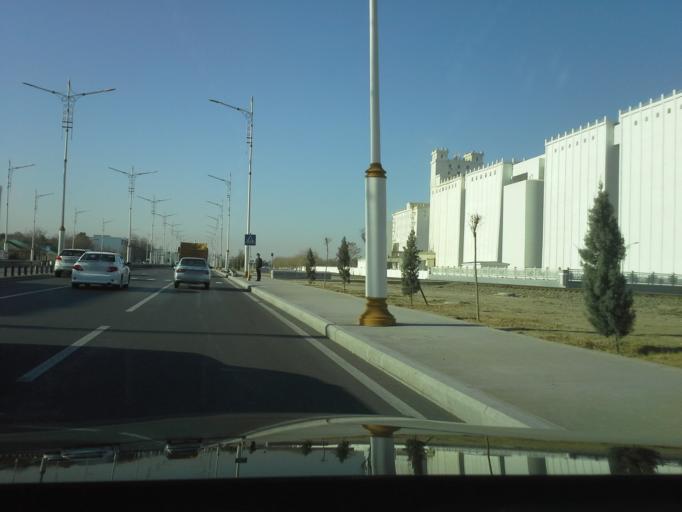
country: TM
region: Ahal
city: Ashgabat
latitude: 37.9543
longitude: 58.3748
